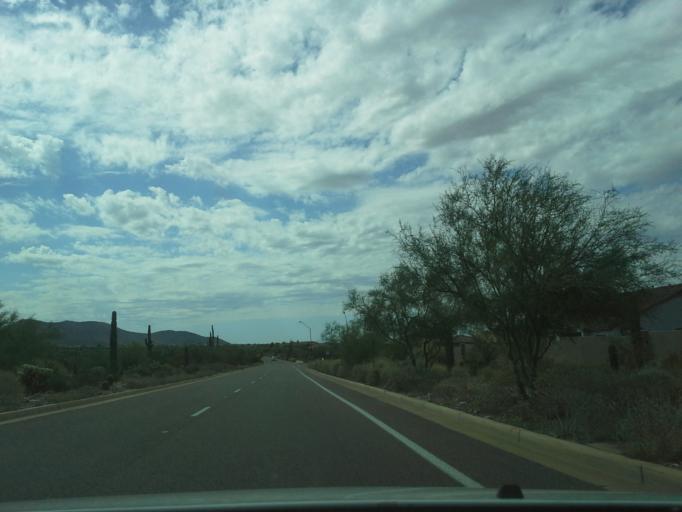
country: US
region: Arizona
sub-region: Maricopa County
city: Paradise Valley
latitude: 33.6551
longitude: -111.8664
